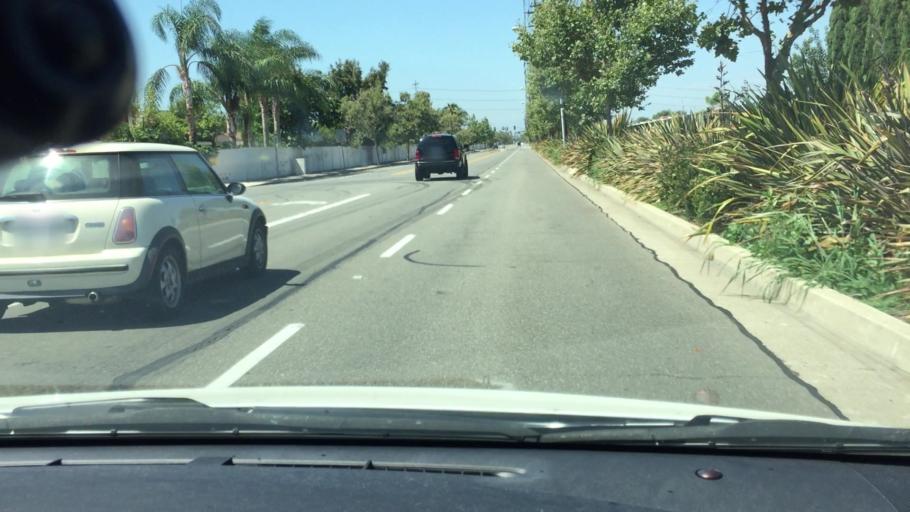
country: US
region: California
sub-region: Orange County
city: Santa Ana
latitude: 33.7027
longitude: -117.8769
